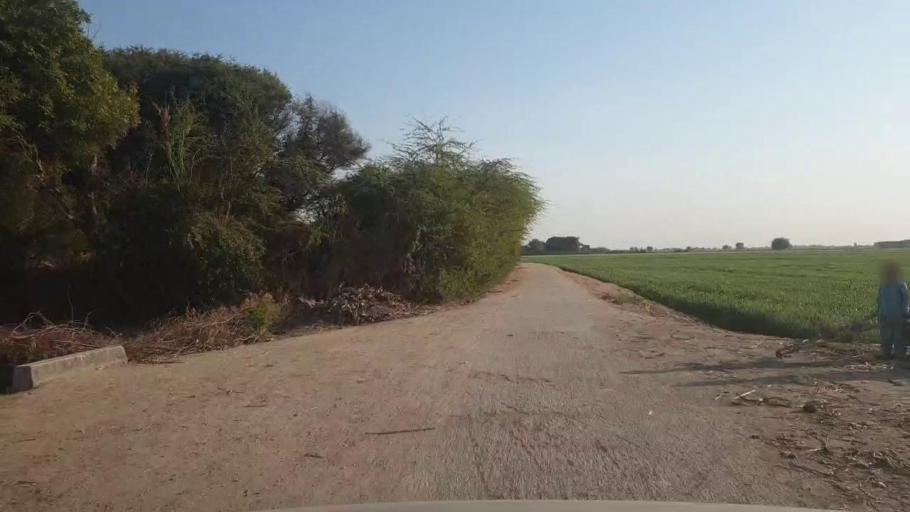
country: PK
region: Sindh
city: Chambar
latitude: 25.2519
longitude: 68.8849
